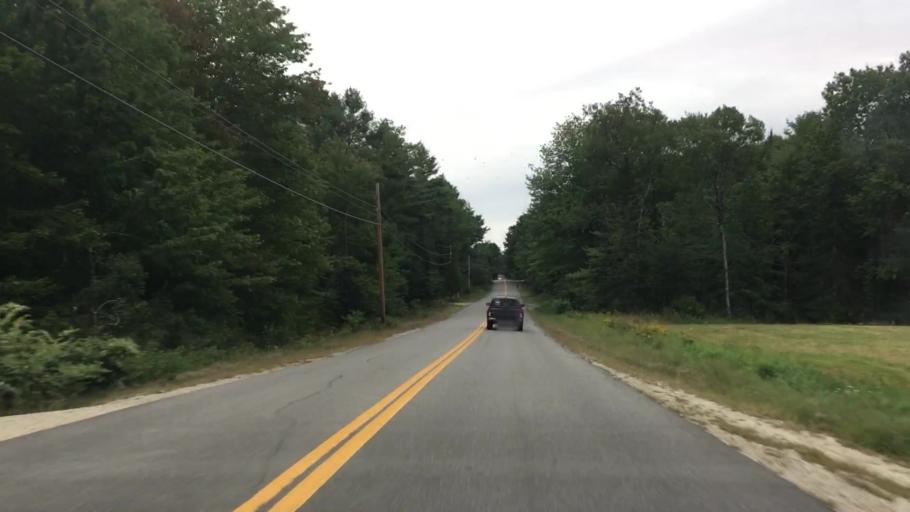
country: US
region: Maine
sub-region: Cumberland County
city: Freeport
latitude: 43.8821
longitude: -70.1635
